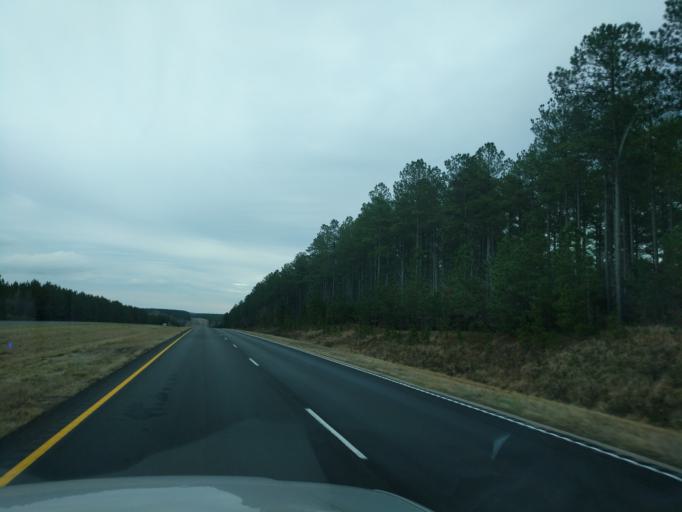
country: US
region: South Carolina
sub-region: Laurens County
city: Clinton
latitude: 34.3673
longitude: -81.9646
